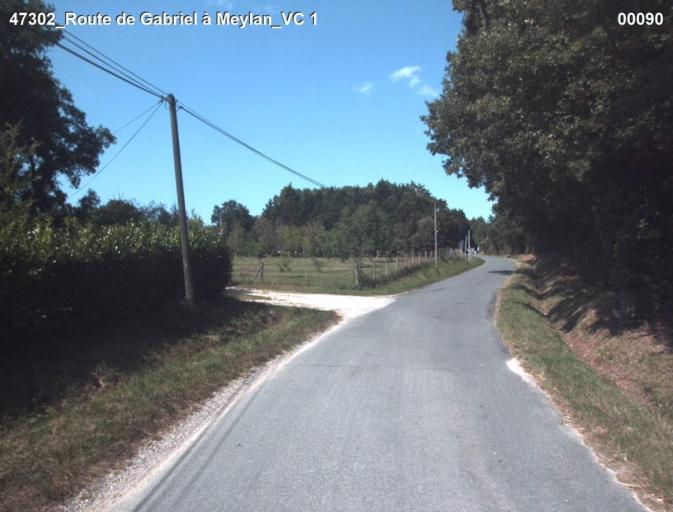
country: FR
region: Aquitaine
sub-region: Departement du Lot-et-Garonne
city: Mezin
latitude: 44.0527
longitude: 0.1422
